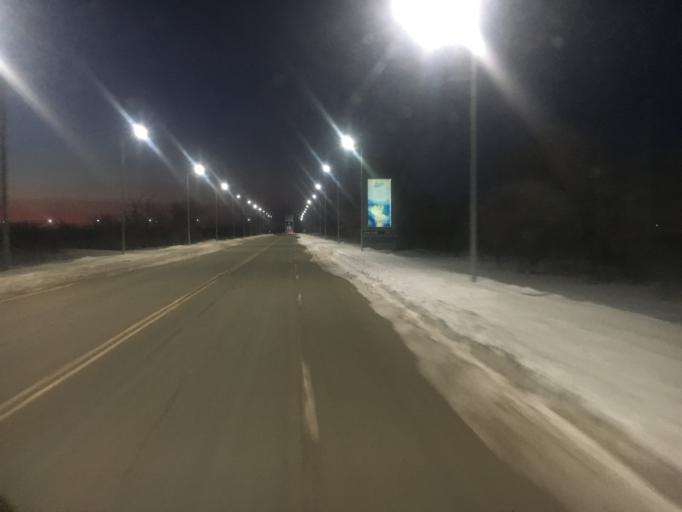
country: KZ
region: Batys Qazaqstan
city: Oral
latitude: 51.1625
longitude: 51.5275
